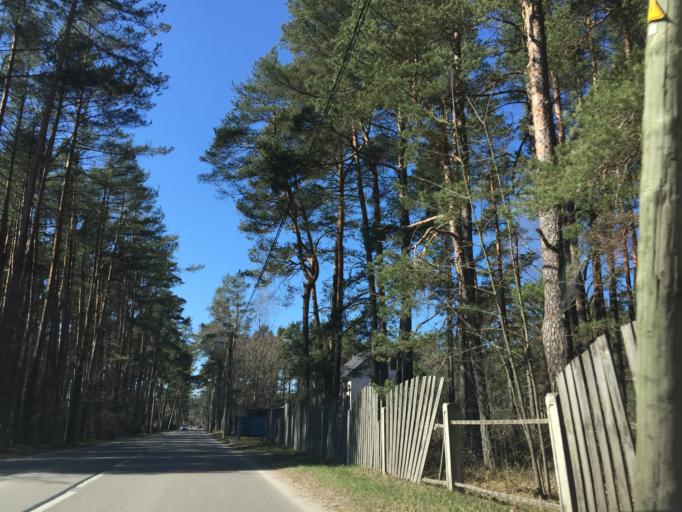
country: LV
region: Jurmala
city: Jurmala
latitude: 56.9429
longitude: 23.7098
